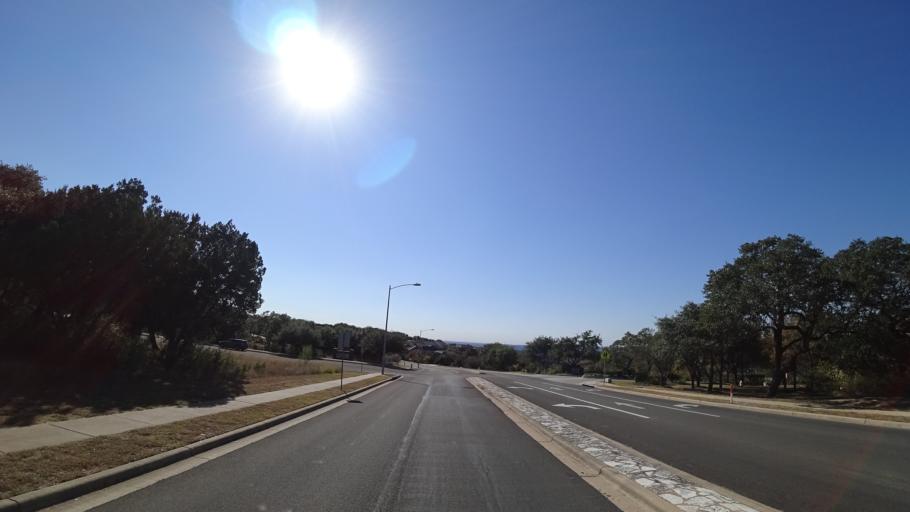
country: US
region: Texas
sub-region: Williamson County
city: Anderson Mill
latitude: 30.3920
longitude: -97.8472
